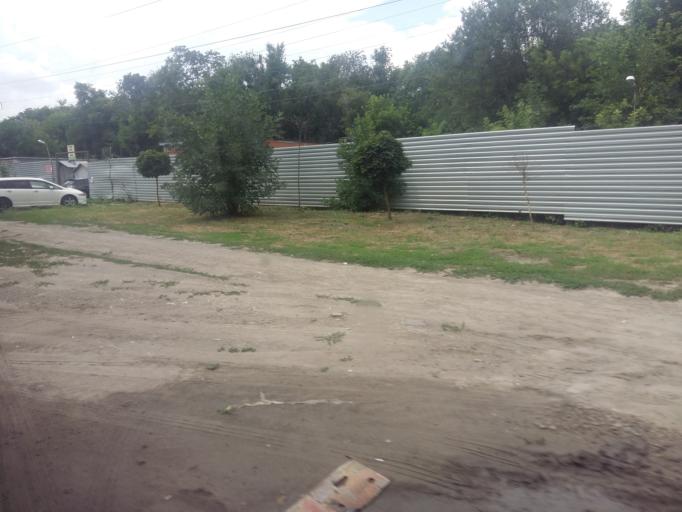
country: RU
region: Rostov
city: Temernik
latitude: 47.2971
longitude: 39.7573
